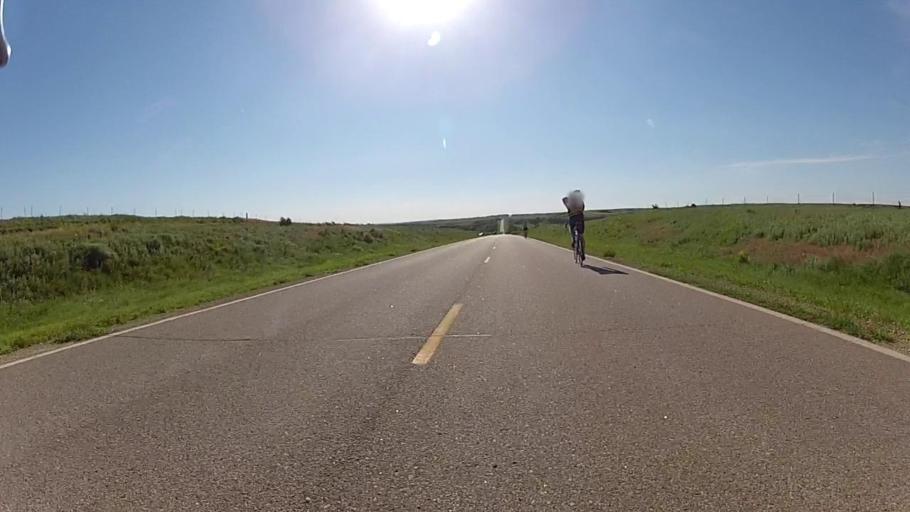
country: US
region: Kansas
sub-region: Barber County
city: Medicine Lodge
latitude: 37.2816
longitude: -98.8828
